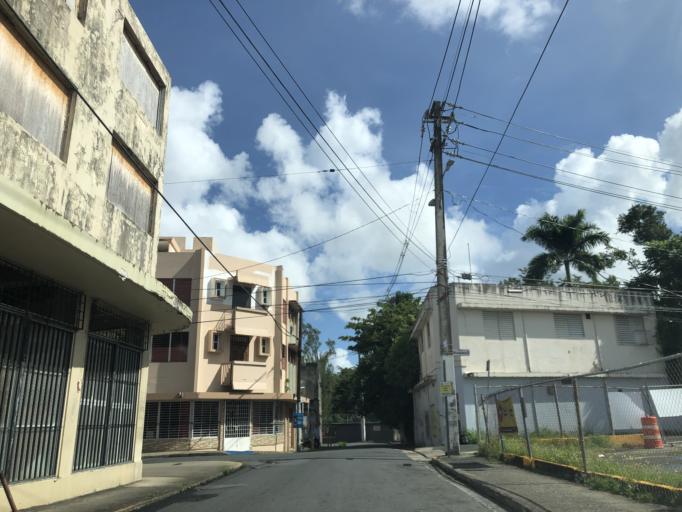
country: PR
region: Trujillo Alto
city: Trujillo Alto
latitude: 18.3996
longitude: -66.0497
